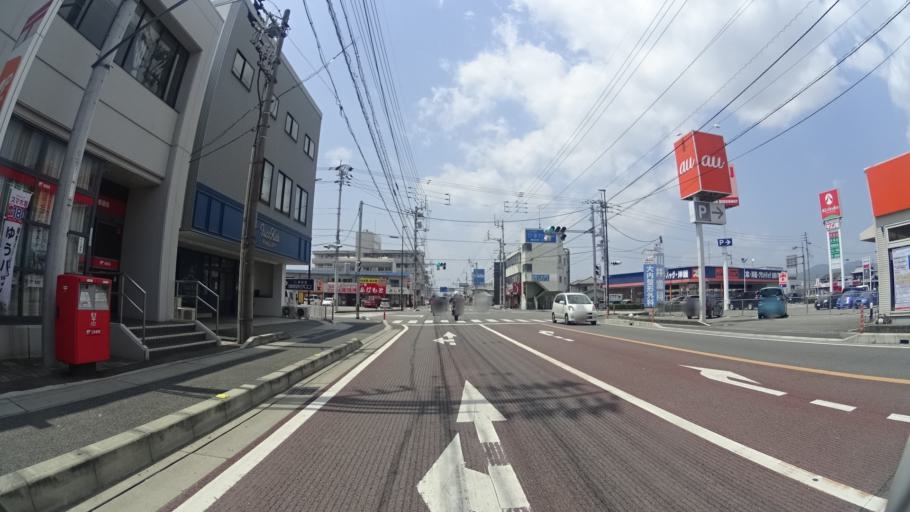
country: JP
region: Tokushima
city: Kamojimacho-jogejima
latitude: 34.0683
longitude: 134.3530
